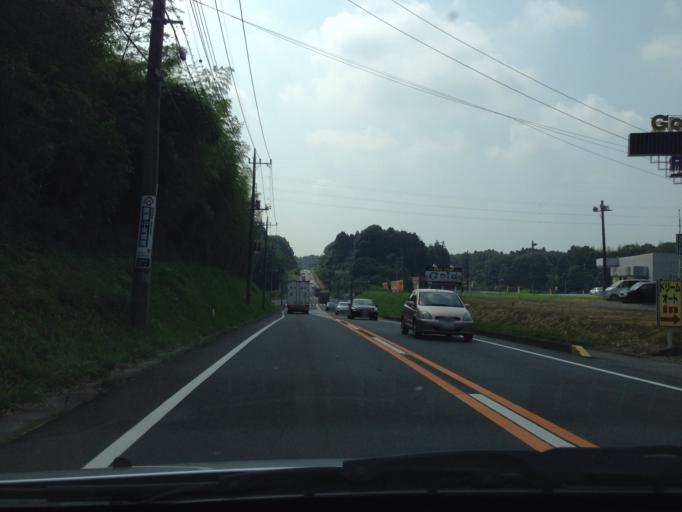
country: JP
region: Ibaraki
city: Inashiki
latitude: 36.0143
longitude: 140.2888
